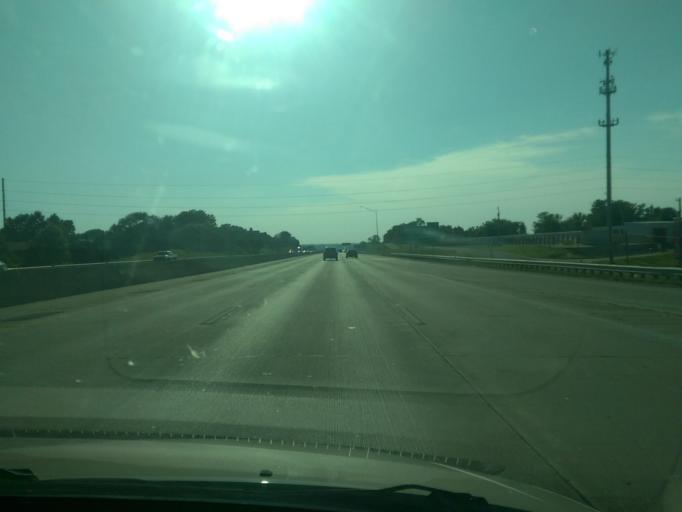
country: US
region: Missouri
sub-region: Jackson County
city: Blue Springs
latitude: 39.0347
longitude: -94.3082
